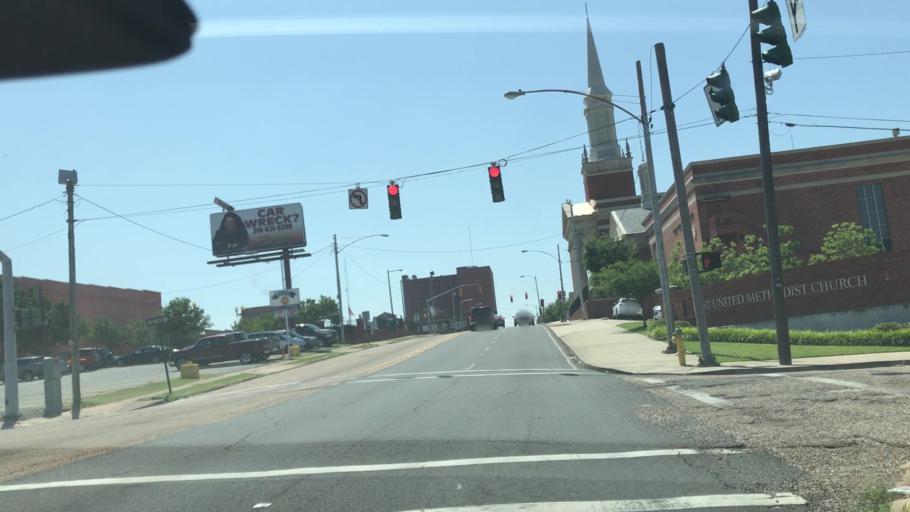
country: US
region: Louisiana
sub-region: Caddo Parish
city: Shreveport
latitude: 32.5117
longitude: -93.7536
